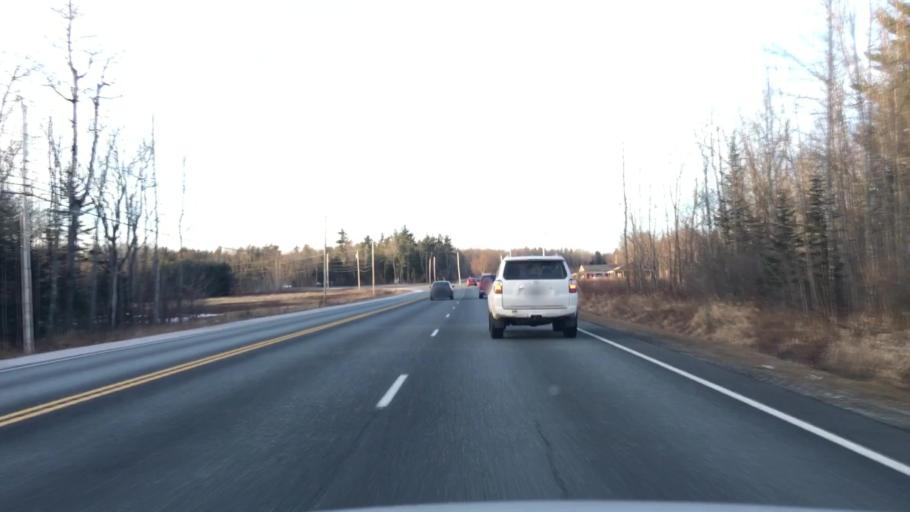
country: US
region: Maine
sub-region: Hancock County
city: Dedham
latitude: 44.6426
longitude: -68.5536
